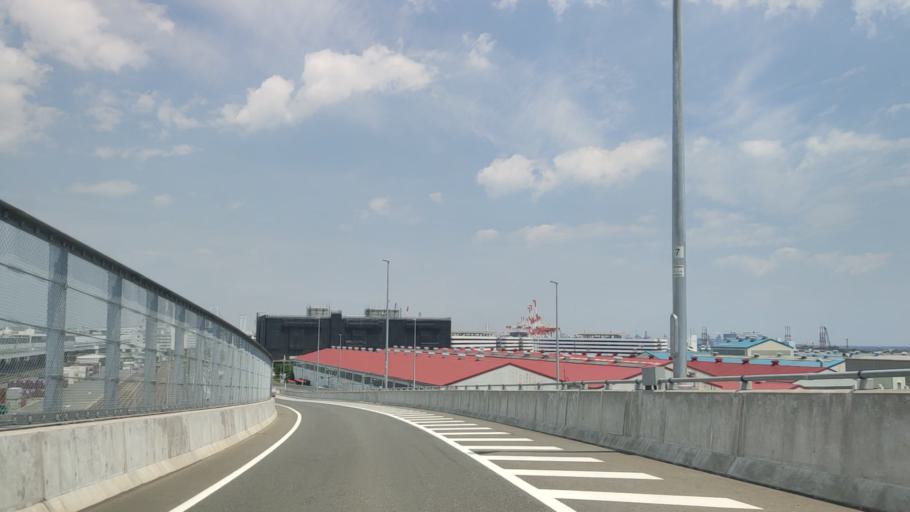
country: JP
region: Kanagawa
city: Yokohama
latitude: 35.4205
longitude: 139.6716
